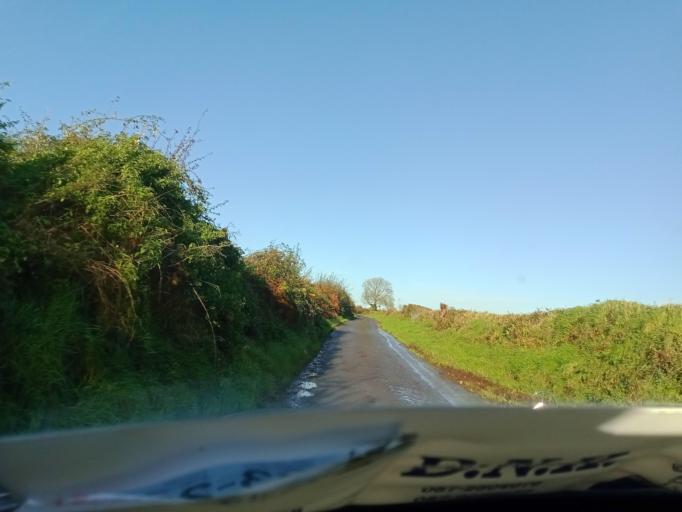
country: IE
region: Munster
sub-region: Waterford
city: Waterford
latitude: 52.2859
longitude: -7.1667
